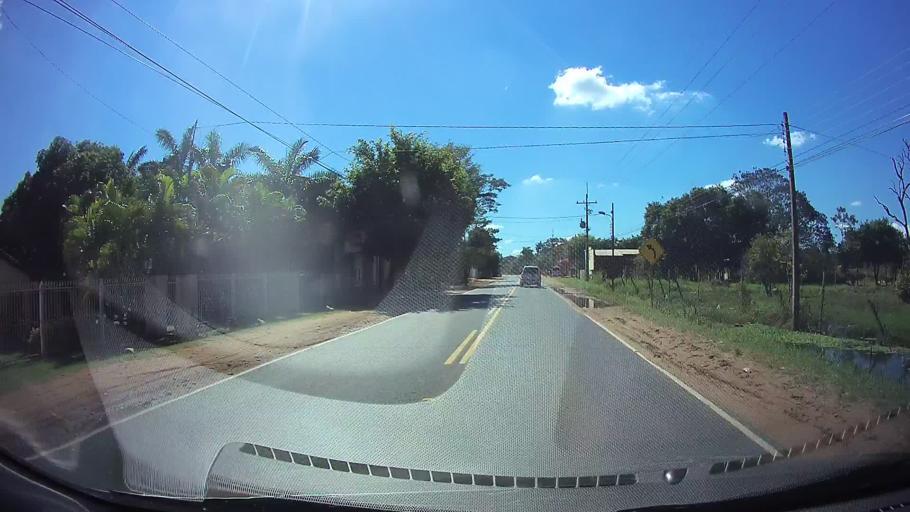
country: PY
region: Central
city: Limpio
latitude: -25.1962
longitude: -57.4641
